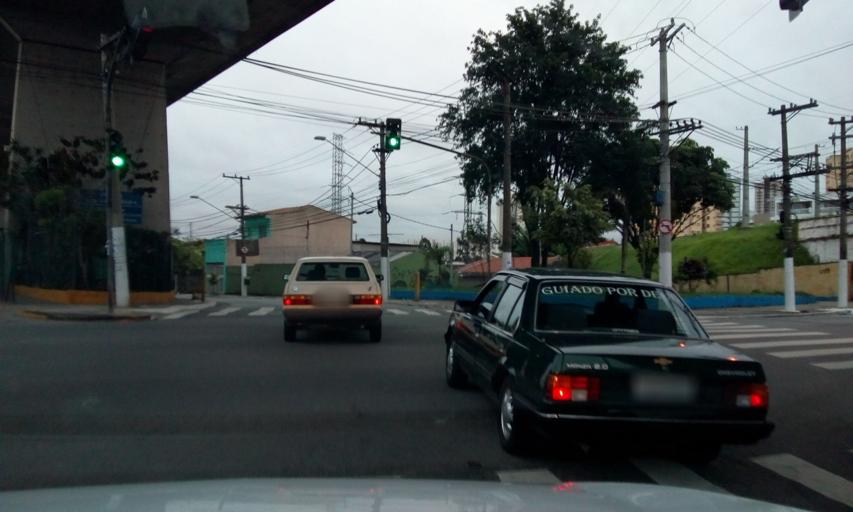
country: BR
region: Sao Paulo
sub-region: Guarulhos
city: Guarulhos
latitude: -23.5298
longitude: -46.5538
